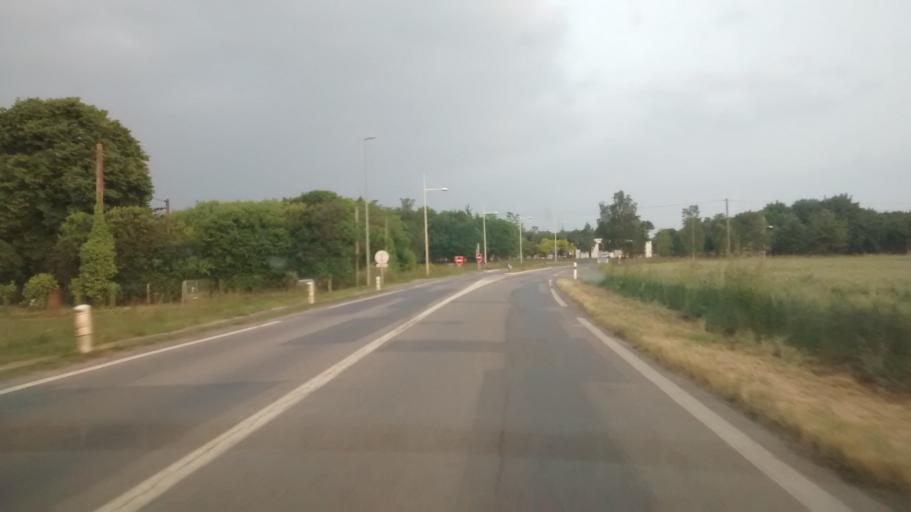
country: FR
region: Brittany
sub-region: Departement du Morbihan
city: Guer
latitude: 47.9334
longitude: -2.1286
